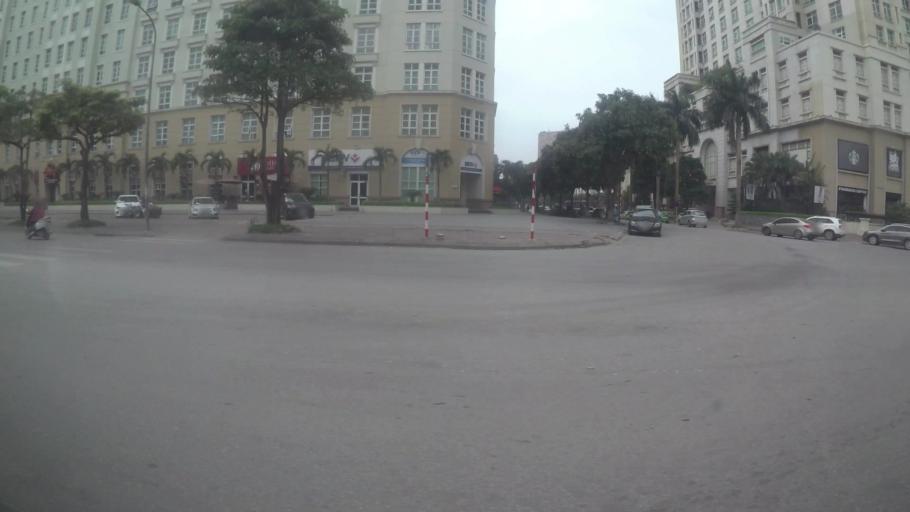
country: VN
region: Ha Noi
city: Cau Dien
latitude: 21.0140
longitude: 105.7771
